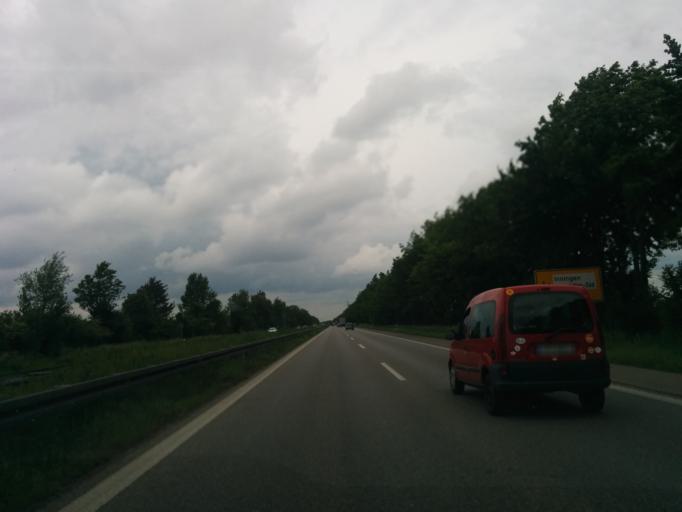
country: DE
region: Bavaria
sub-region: Swabia
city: Konigsbrunn
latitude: 48.2995
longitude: 10.8792
